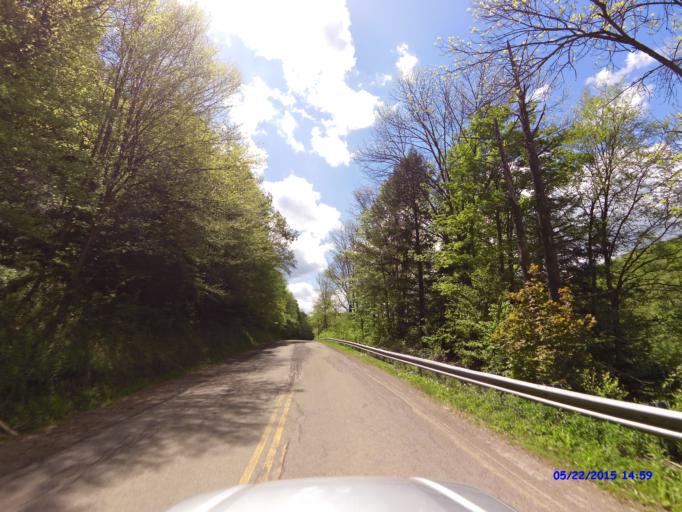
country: US
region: New York
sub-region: Erie County
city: Springville
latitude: 42.3628
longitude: -78.6426
